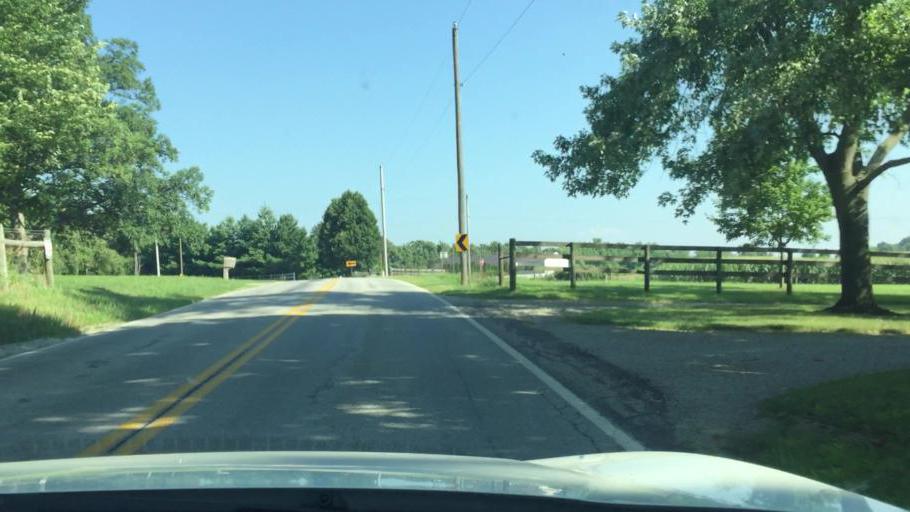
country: US
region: Ohio
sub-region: Clark County
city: Northridge
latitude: 39.9835
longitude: -83.6818
